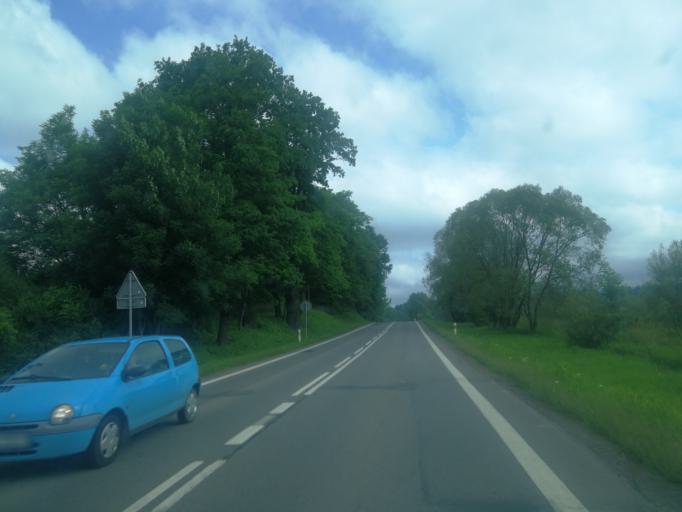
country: PL
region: Subcarpathian Voivodeship
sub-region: Powiat leski
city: Lesko
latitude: 49.4838
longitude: 22.3233
